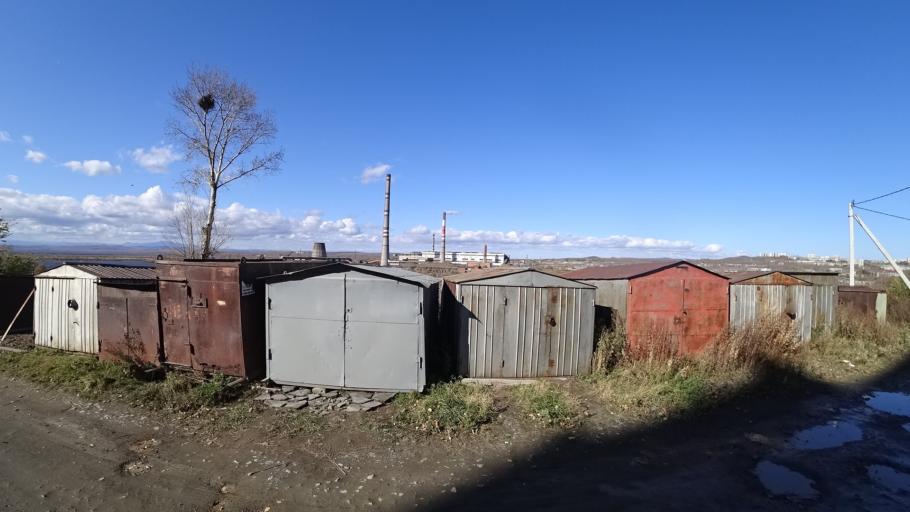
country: RU
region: Khabarovsk Krai
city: Amursk
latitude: 50.2185
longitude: 136.8923
